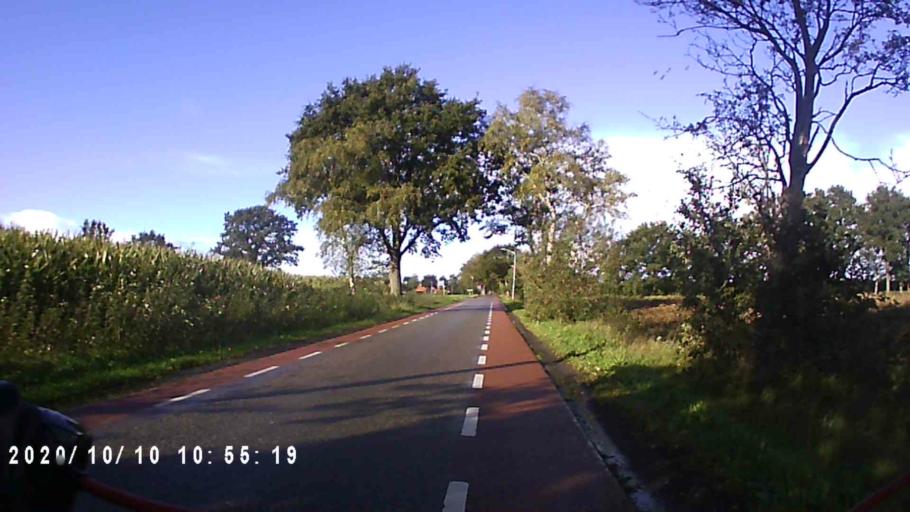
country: NL
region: Friesland
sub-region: Gemeente Achtkarspelen
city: Surhuisterveen
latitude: 53.1545
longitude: 6.2080
